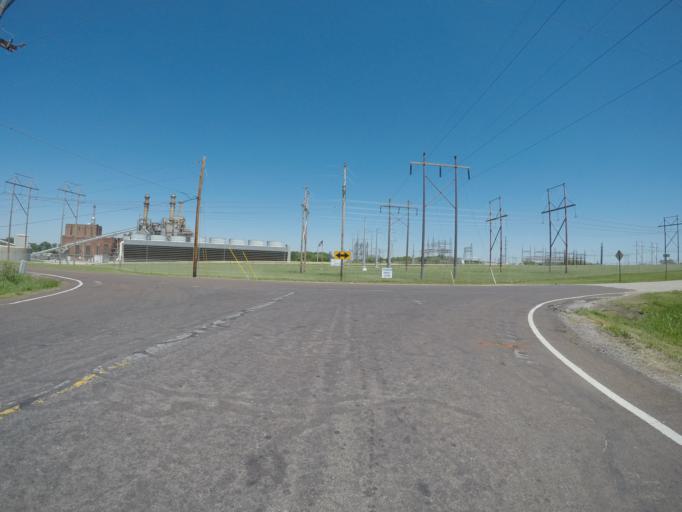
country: US
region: Kansas
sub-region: Shawnee County
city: Topeka
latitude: 39.0514
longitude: -95.5663
